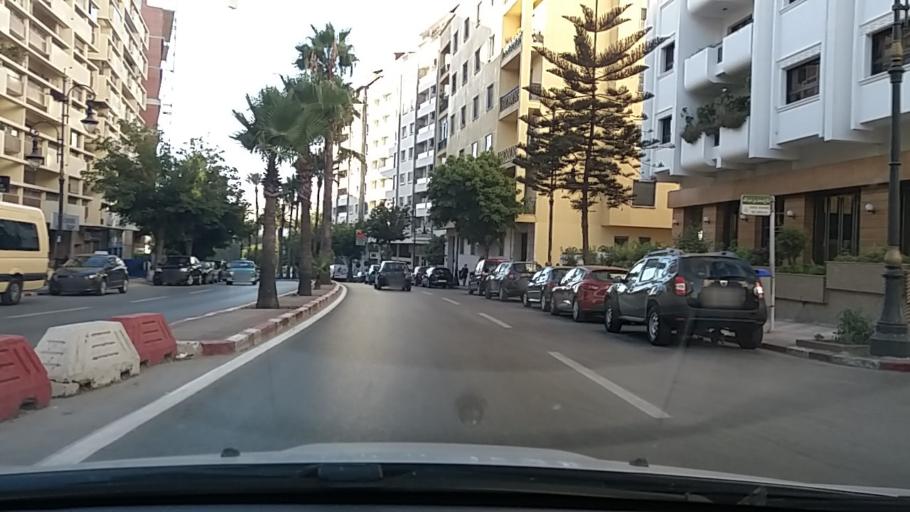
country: MA
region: Tanger-Tetouan
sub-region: Tanger-Assilah
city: Tangier
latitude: 35.7823
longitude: -5.8211
